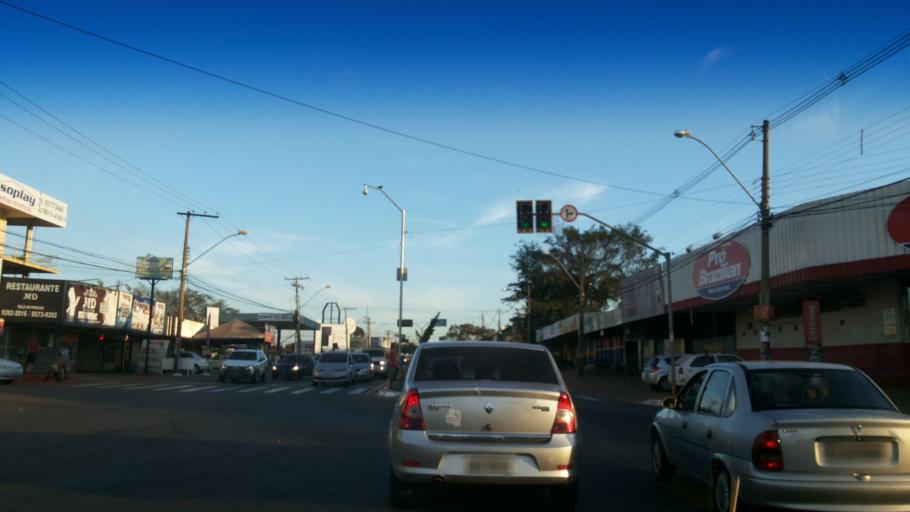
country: BR
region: Goias
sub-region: Goiania
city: Goiania
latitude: -16.6228
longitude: -49.2841
